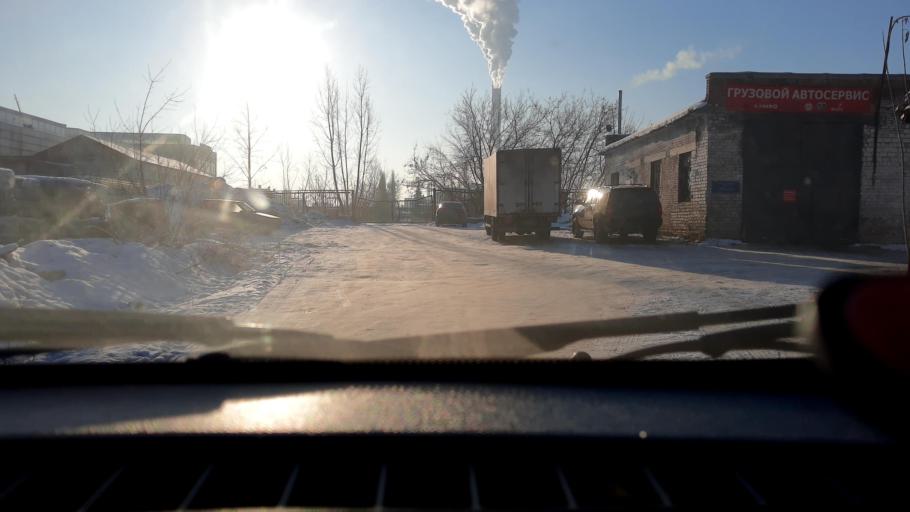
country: RU
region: Bashkortostan
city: Ufa
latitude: 54.7971
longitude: 56.1207
